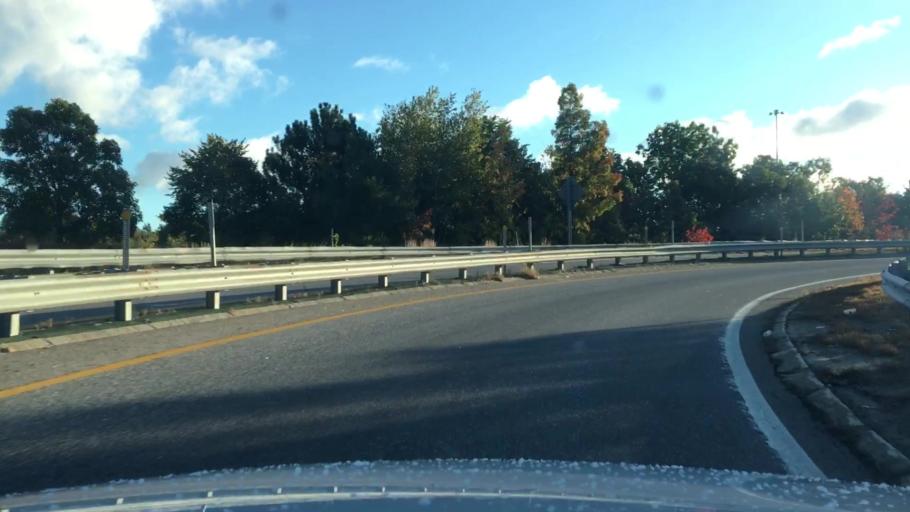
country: US
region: Maine
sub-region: Cumberland County
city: Portland
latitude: 43.6572
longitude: -70.2855
